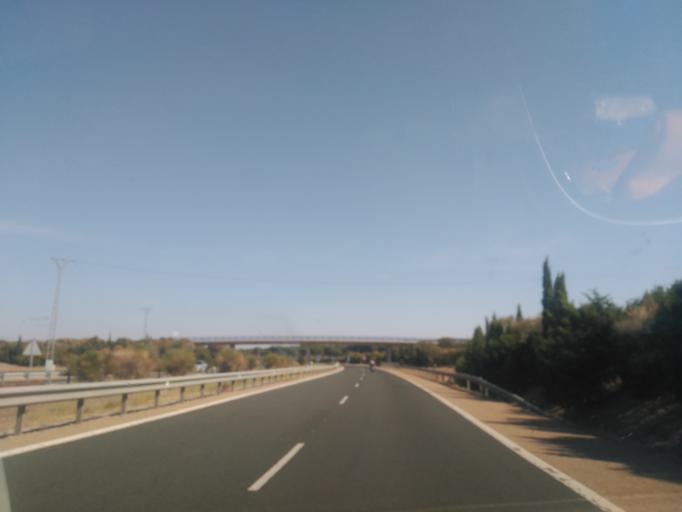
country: ES
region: Castille and Leon
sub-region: Provincia de Valladolid
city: Tudela de Duero
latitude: 41.5873
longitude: -4.5569
